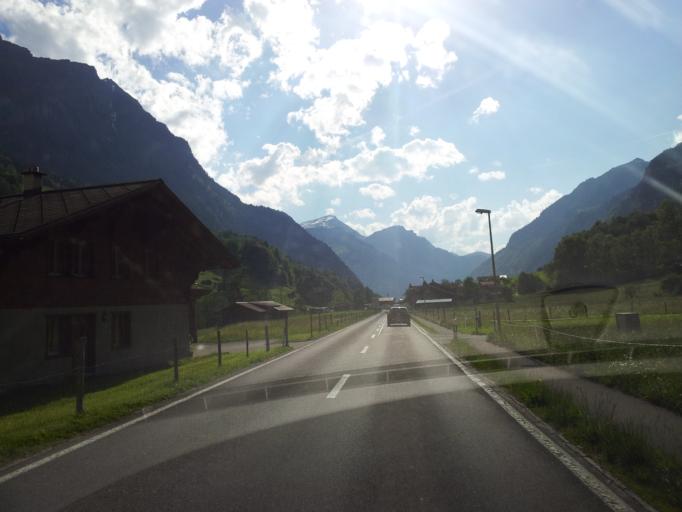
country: CH
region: Bern
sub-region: Interlaken-Oberhasli District
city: Grindelwald
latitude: 46.6363
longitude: 7.9825
